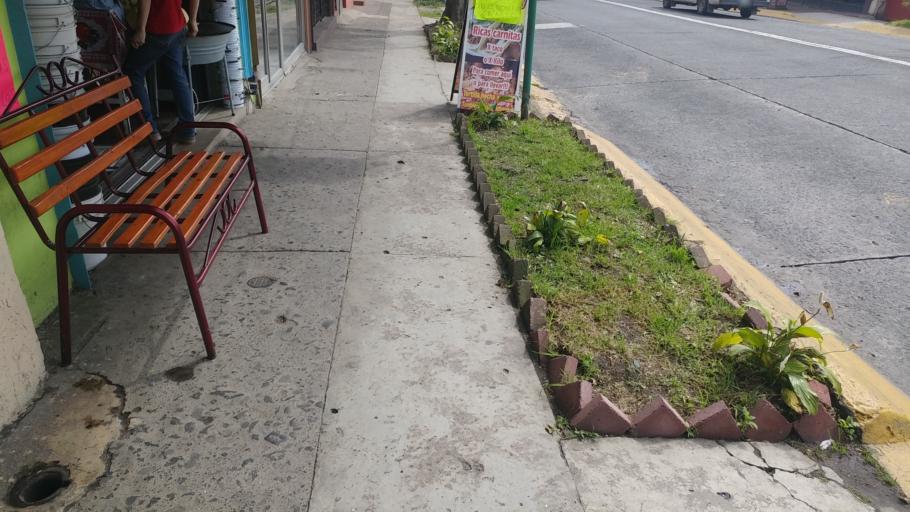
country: MX
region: Veracruz
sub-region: Xalapa
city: Xalapa de Enriquez
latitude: 19.5272
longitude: -96.9103
